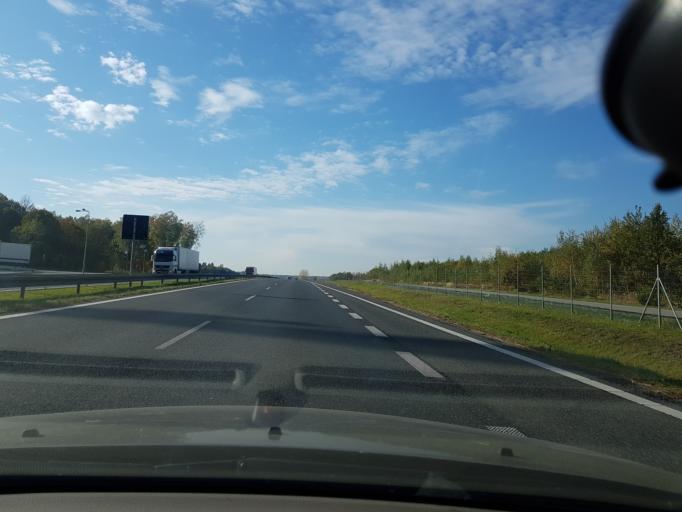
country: PL
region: Masovian Voivodeship
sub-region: Powiat zyrardowski
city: Mszczonow
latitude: 51.9513
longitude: 20.4907
